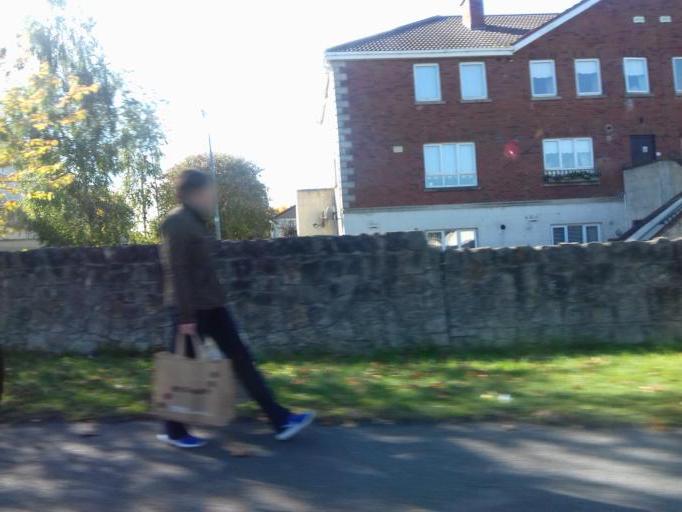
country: IE
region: Leinster
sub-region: An Mhi
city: Ashbourne
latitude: 53.5159
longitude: -6.4057
